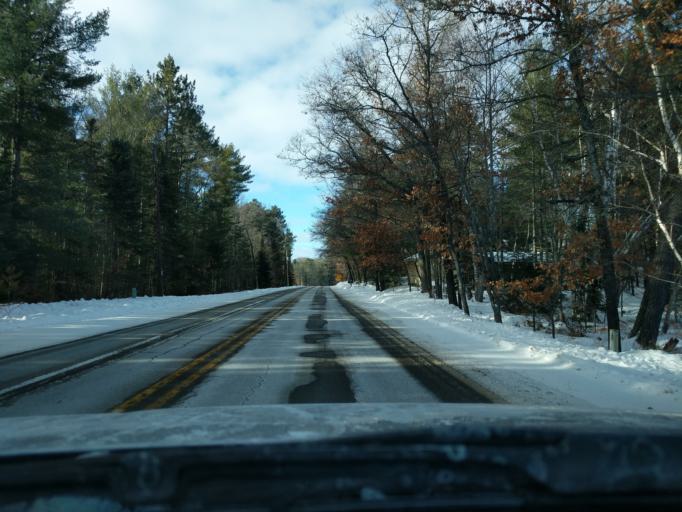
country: US
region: Wisconsin
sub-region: Vilas County
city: Eagle River
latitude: 45.7727
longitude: -89.0713
